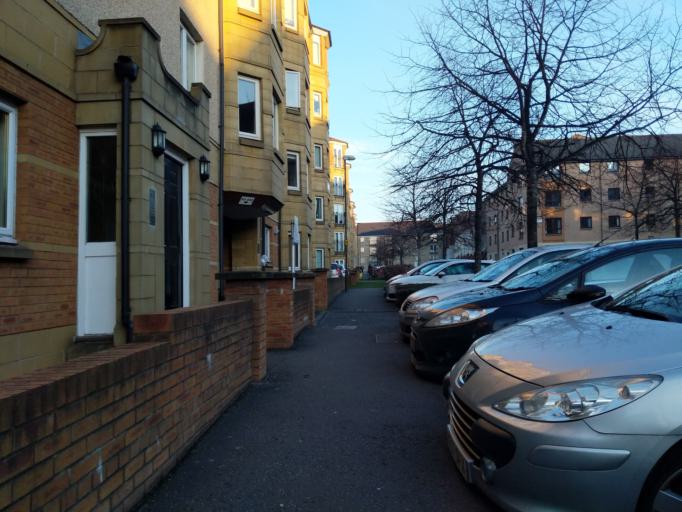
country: GB
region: Scotland
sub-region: Edinburgh
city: Edinburgh
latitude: 55.9439
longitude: -3.2223
